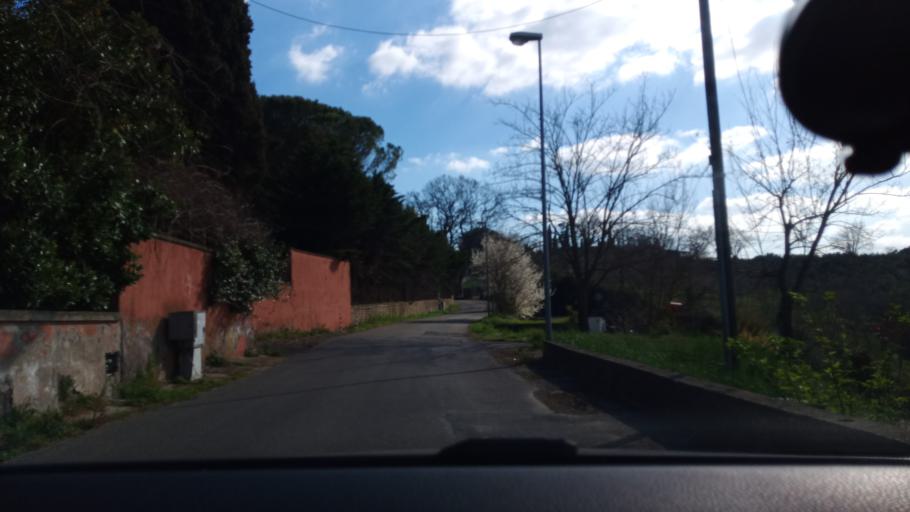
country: IT
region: Latium
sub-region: Citta metropolitana di Roma Capitale
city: Torrita Tiberina
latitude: 42.2439
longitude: 12.6141
